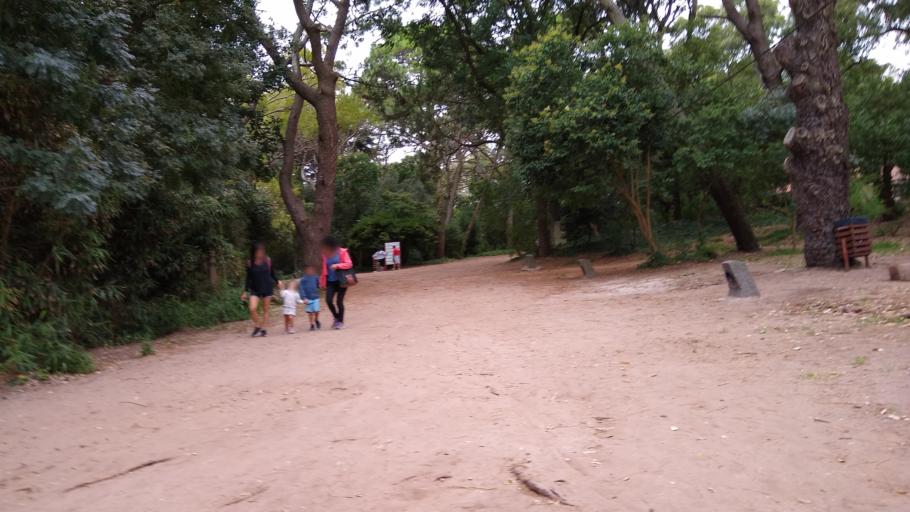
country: AR
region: Buenos Aires
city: Villa Gesell
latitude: -37.2522
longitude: -56.9634
